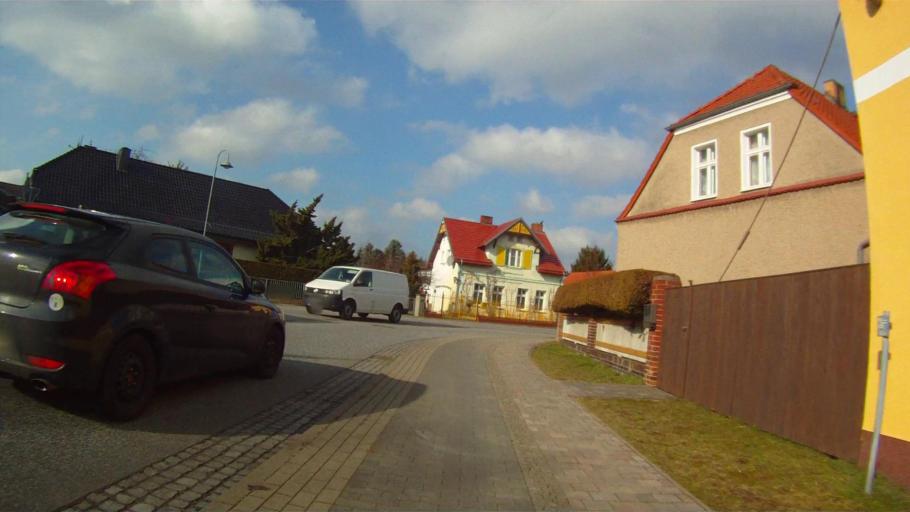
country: DE
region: Berlin
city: Schmockwitz
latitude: 52.3699
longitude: 13.6982
